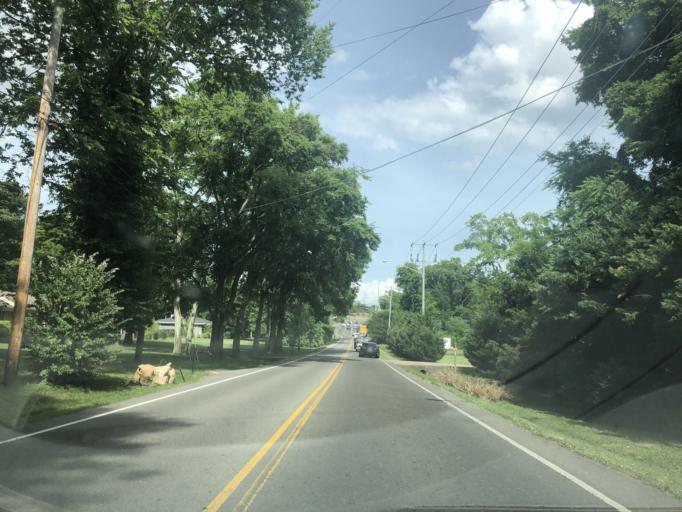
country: US
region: Tennessee
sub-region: Davidson County
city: Oak Hill
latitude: 36.0868
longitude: -86.7757
